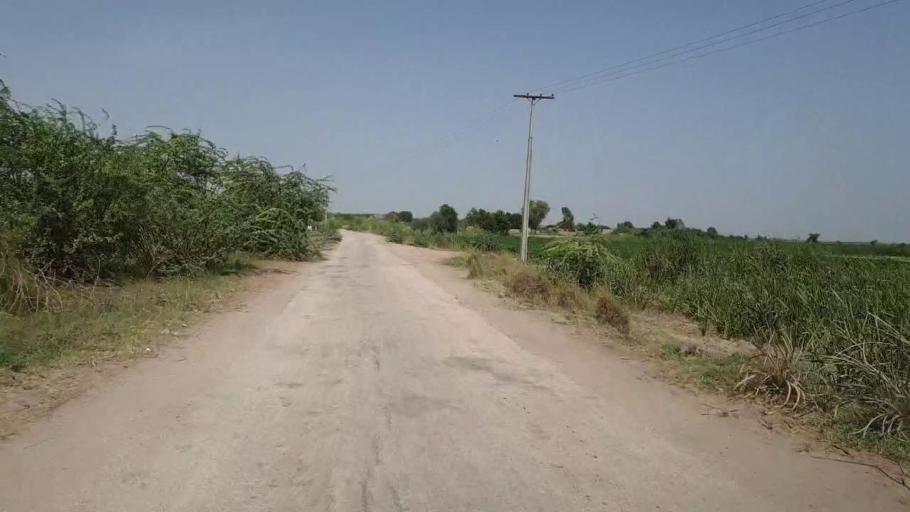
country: PK
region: Sindh
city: Jam Sahib
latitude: 26.4093
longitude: 68.9044
